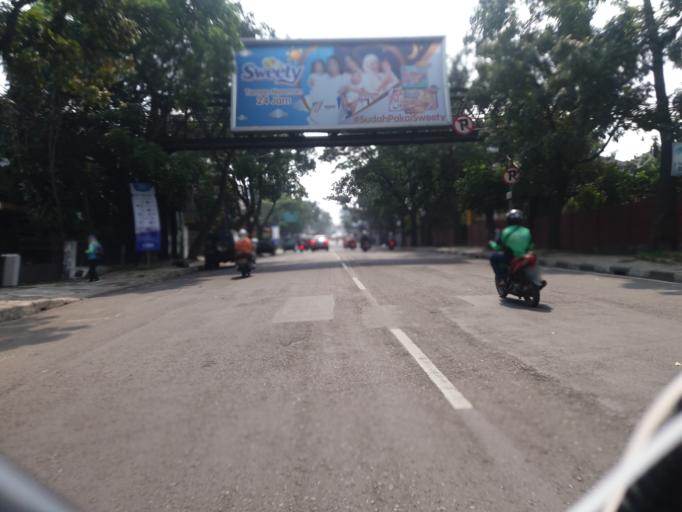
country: ID
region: West Java
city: Bandung
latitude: -6.9084
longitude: 107.5977
